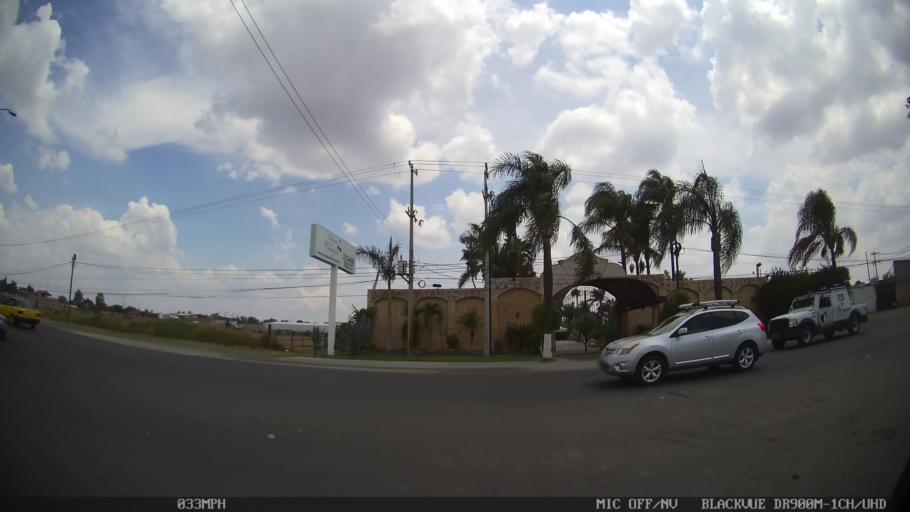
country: MX
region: Jalisco
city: Tonala
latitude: 20.6691
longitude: -103.2325
